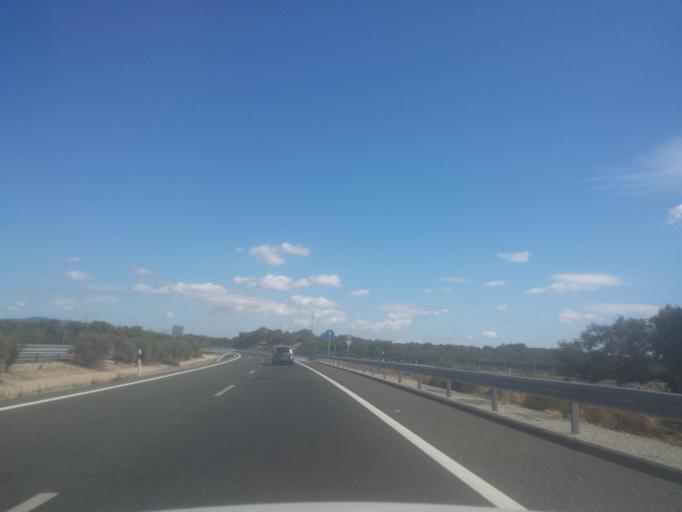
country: ES
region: Andalusia
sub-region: Provincia de Huelva
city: Santa Olalla del Cala
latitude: 37.9041
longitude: -6.2134
